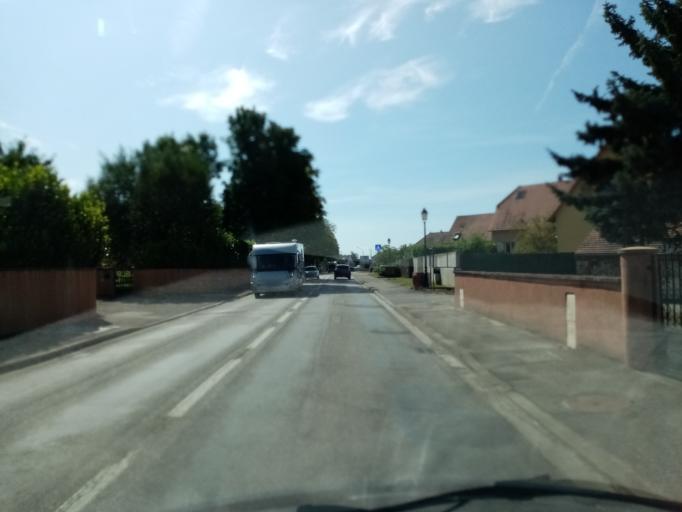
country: FR
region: Alsace
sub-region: Departement du Haut-Rhin
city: Houssen
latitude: 48.1291
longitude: 7.3589
